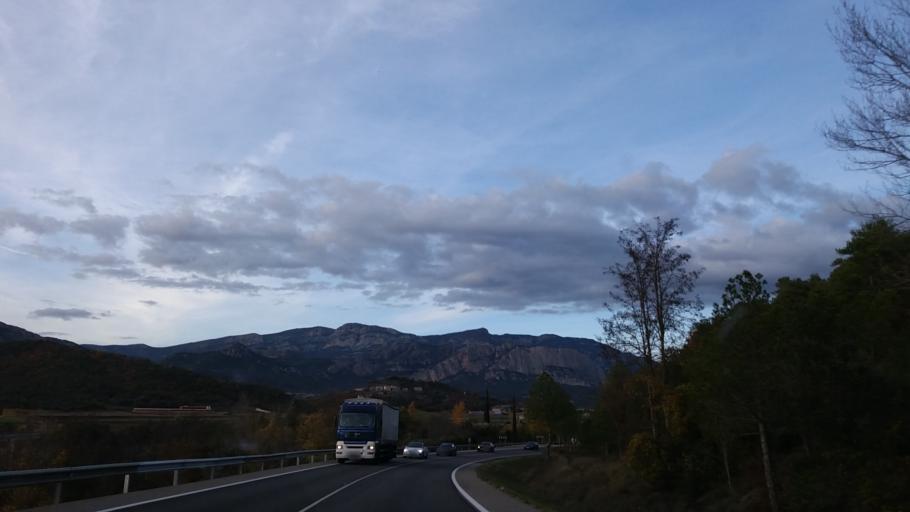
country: ES
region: Catalonia
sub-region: Provincia de Lleida
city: Oliana
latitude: 42.0309
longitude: 1.2943
